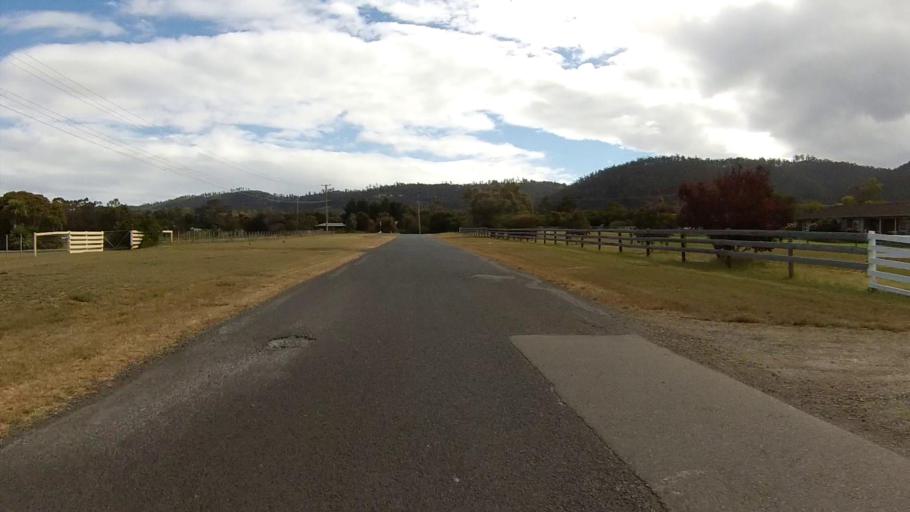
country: AU
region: Tasmania
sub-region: Clarence
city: Acton Park
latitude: -42.8654
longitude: 147.4840
